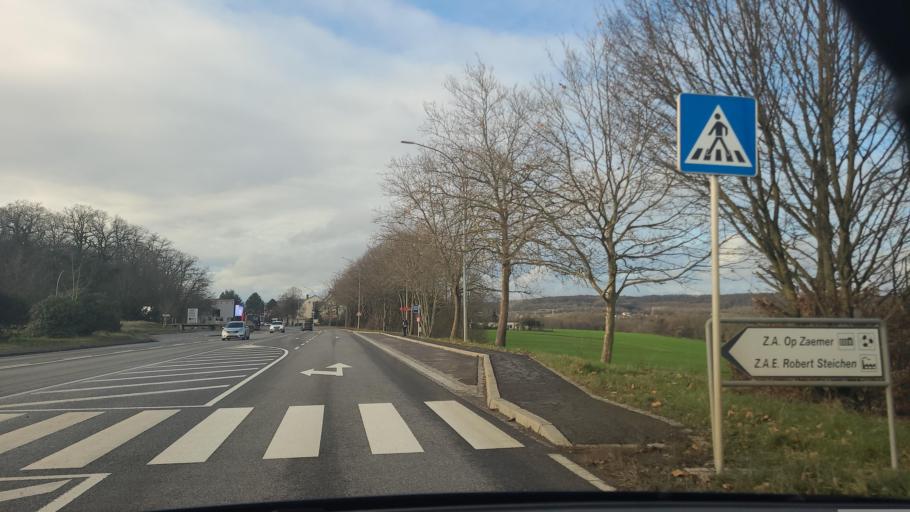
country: LU
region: Luxembourg
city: Hautcharage
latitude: 49.5740
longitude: 5.9313
